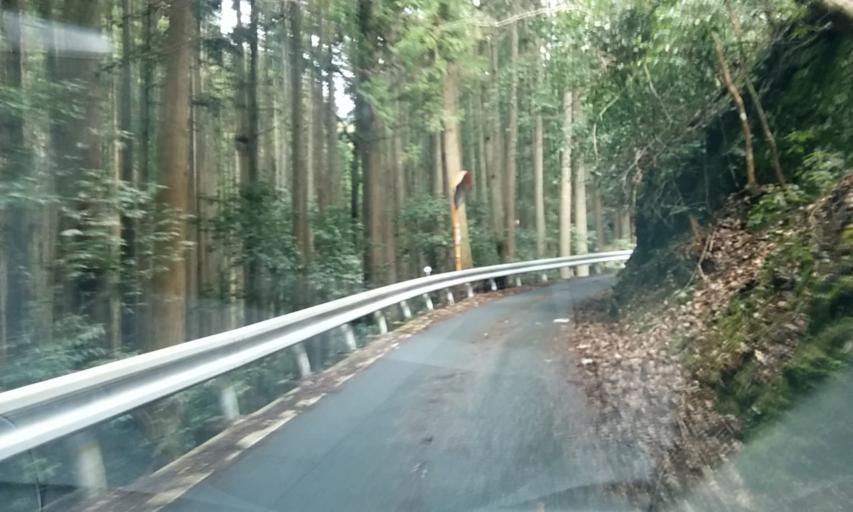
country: JP
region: Kyoto
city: Kameoka
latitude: 35.1138
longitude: 135.4319
